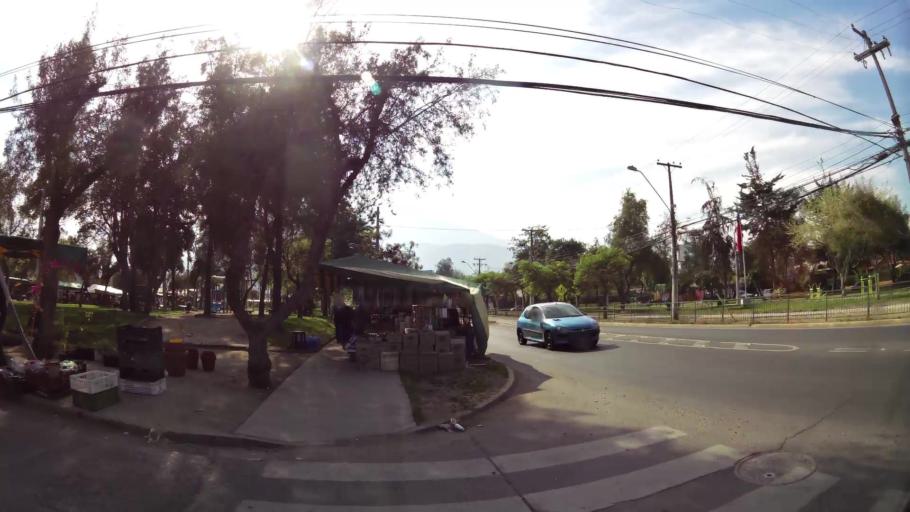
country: CL
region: Santiago Metropolitan
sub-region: Provincia de Cordillera
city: Puente Alto
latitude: -33.5596
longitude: -70.5617
